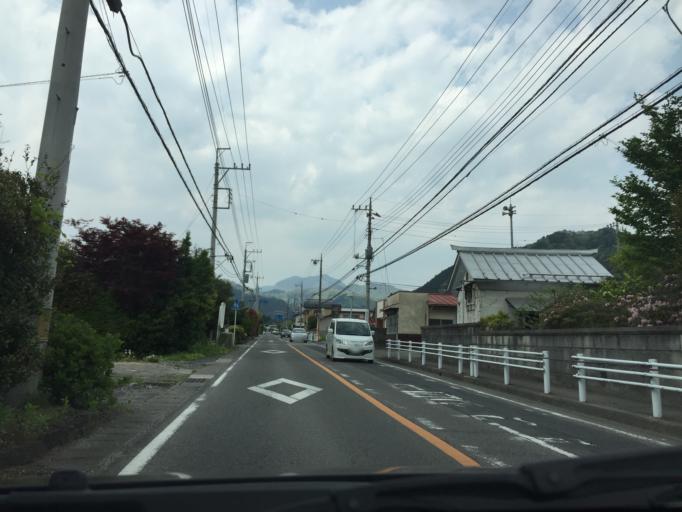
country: JP
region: Tochigi
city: Imaichi
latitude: 36.7819
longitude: 139.7119
